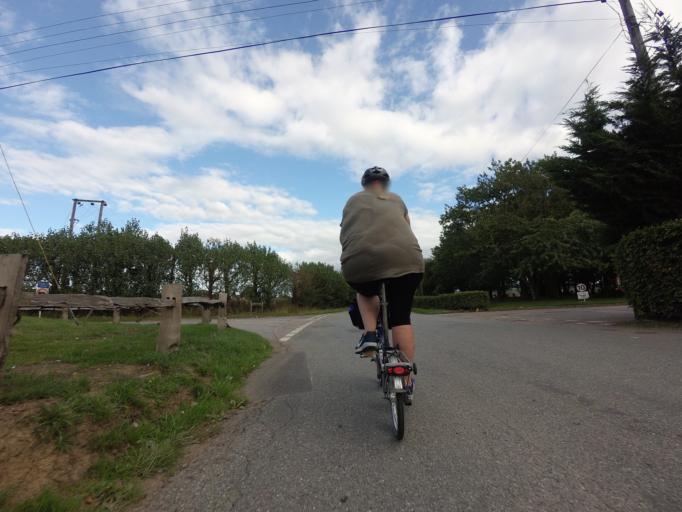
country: GB
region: England
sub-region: Kent
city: Marden
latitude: 51.2118
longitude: 0.4971
